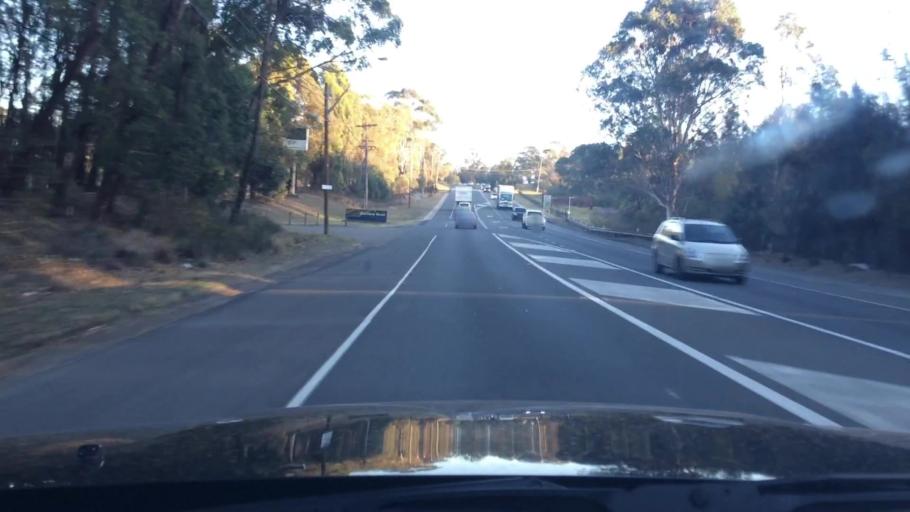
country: AU
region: New South Wales
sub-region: Fairfield
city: Carramar
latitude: -33.8963
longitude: 150.9725
